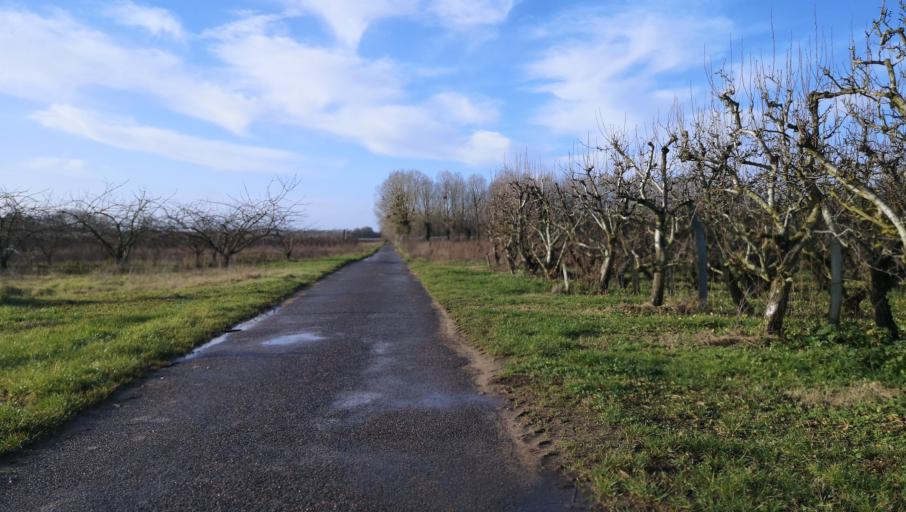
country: FR
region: Centre
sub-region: Departement du Loiret
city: Saint-Hilaire-Saint-Mesmin
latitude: 47.8711
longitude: 1.8272
